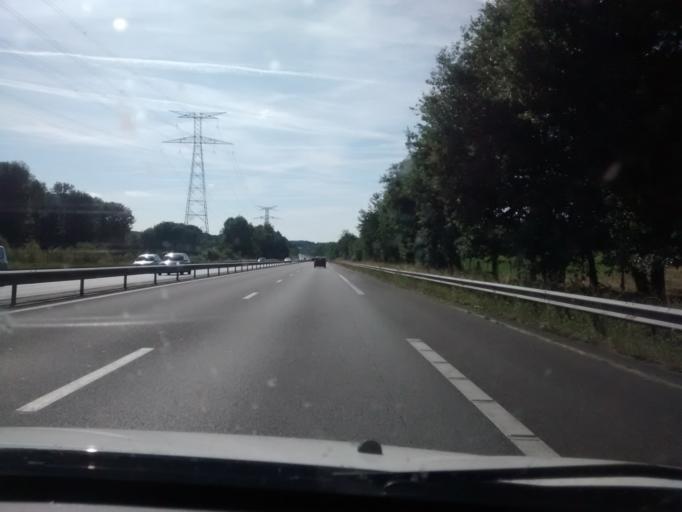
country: FR
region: Pays de la Loire
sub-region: Departement de la Mayenne
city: Saint-Pierre-la-Cour
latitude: 48.0861
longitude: -1.0587
